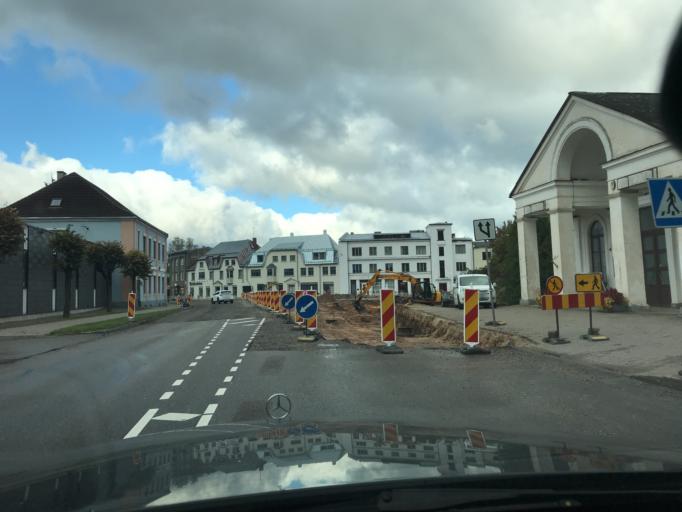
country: EE
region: Valgamaa
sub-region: Torva linn
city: Torva
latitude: 58.0021
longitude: 25.9241
